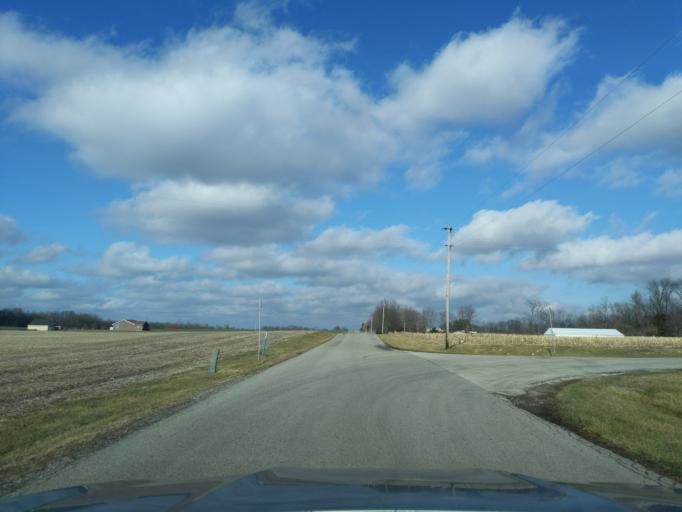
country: US
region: Indiana
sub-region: Decatur County
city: Greensburg
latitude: 39.2786
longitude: -85.4472
